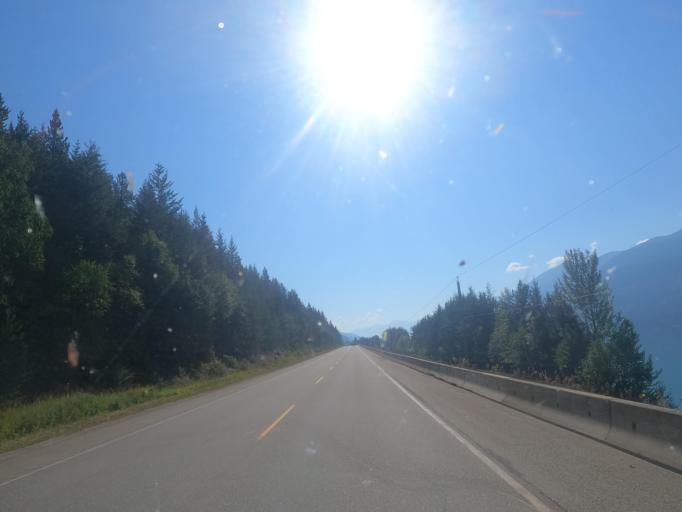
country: CA
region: Alberta
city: Jasper Park Lodge
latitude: 52.9596
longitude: -118.9036
